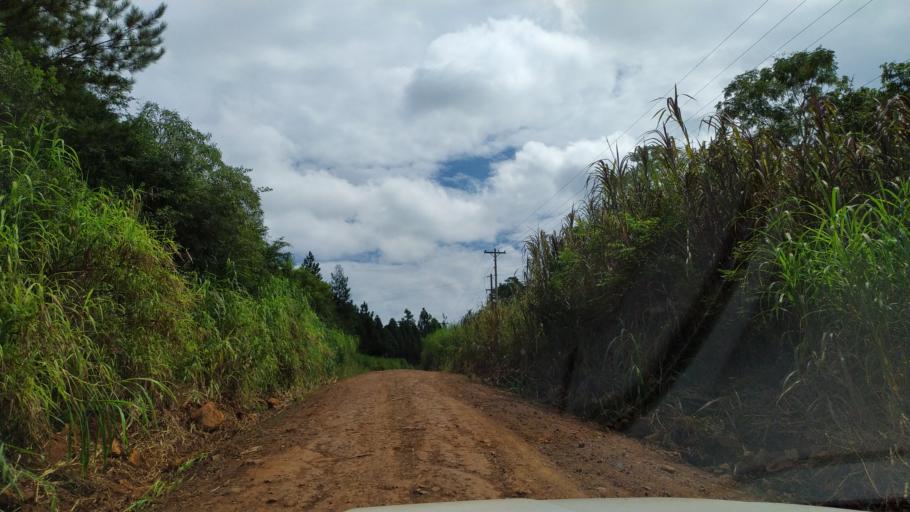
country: AR
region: Misiones
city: Puerto Piray
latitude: -26.5362
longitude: -54.6434
